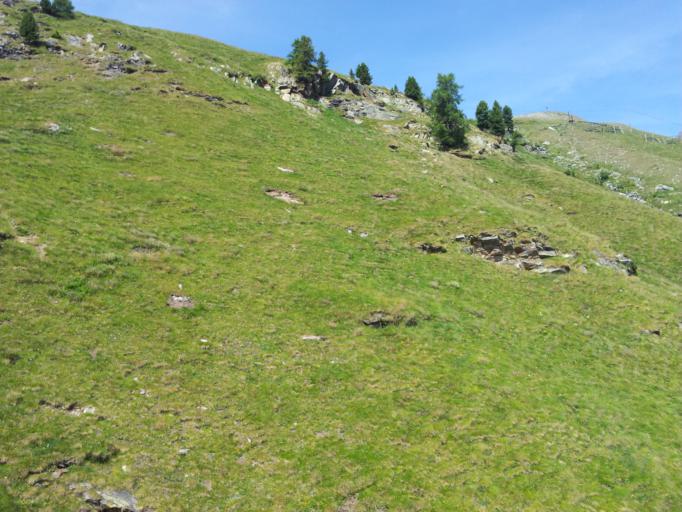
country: CH
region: Valais
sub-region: Visp District
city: Zermatt
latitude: 45.9977
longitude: 7.7224
